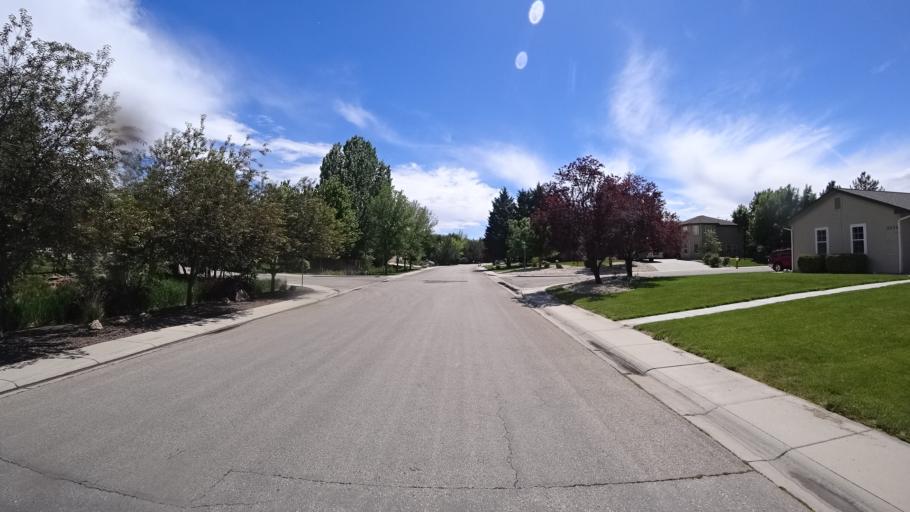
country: US
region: Idaho
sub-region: Ada County
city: Meridian
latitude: 43.5731
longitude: -116.3253
